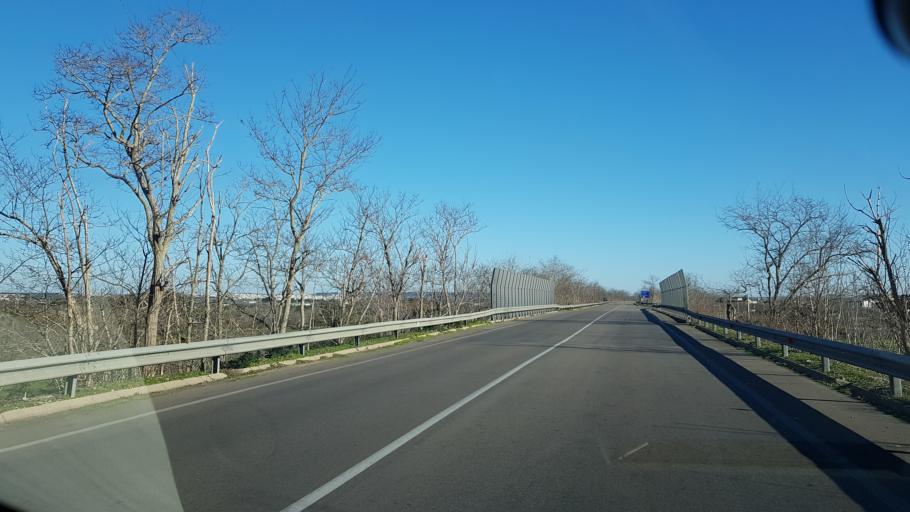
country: IT
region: Apulia
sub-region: Provincia di Lecce
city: Taviano
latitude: 39.9960
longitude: 18.0908
